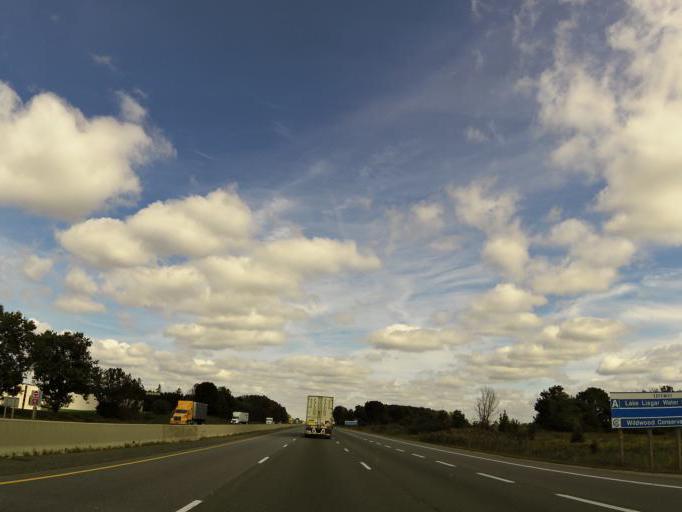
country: CA
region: Ontario
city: Ingersoll
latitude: 43.0143
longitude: -80.8742
